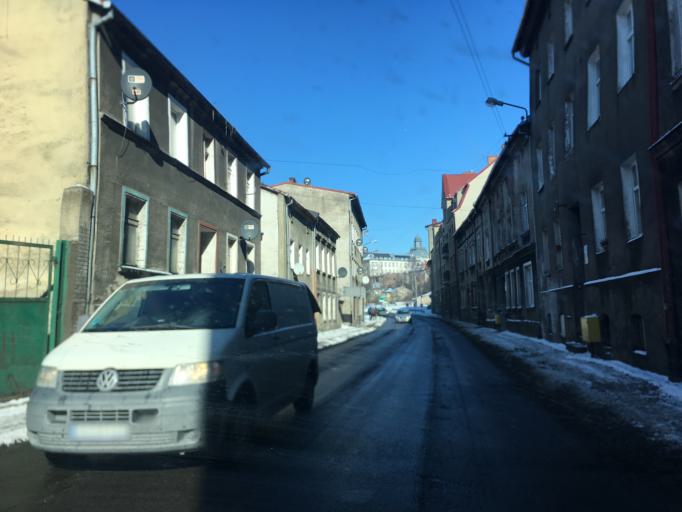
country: PL
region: Pomeranian Voivodeship
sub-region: Slupsk
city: Slupsk
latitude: 54.4654
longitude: 17.0419
